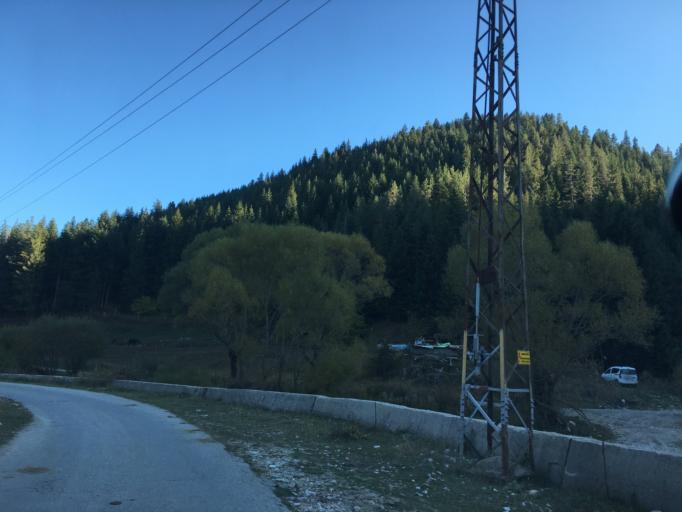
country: BG
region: Smolyan
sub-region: Obshtina Borino
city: Borino
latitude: 41.5829
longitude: 24.3932
